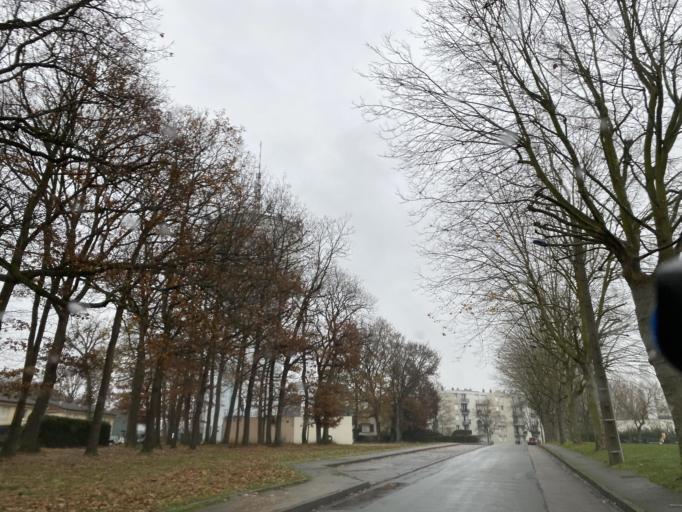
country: FR
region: Haute-Normandie
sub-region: Departement de l'Eure
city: Evreux
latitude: 49.0299
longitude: 1.1687
